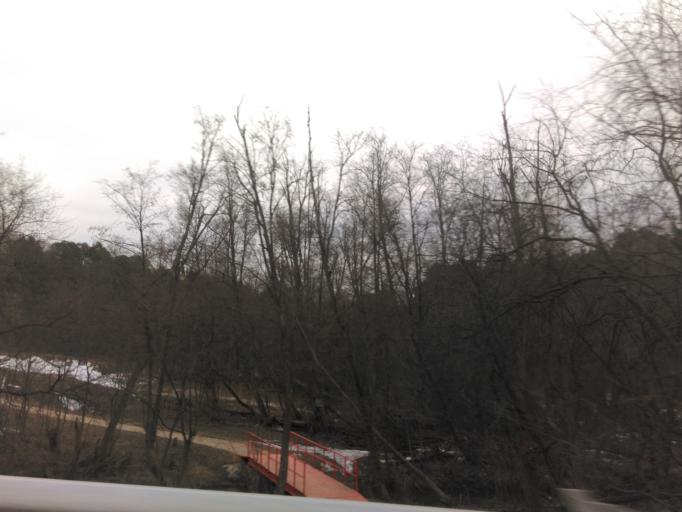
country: RU
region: Moskovskaya
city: Barvikha
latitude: 55.7393
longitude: 37.2735
